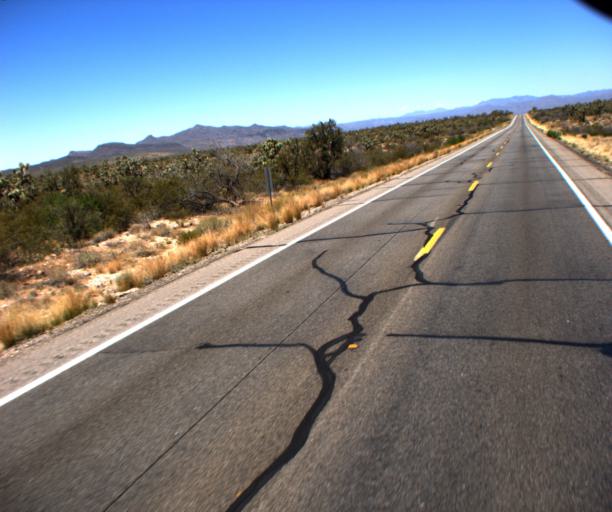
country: US
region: Arizona
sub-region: Yavapai County
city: Congress
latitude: 34.2492
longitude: -113.0812
